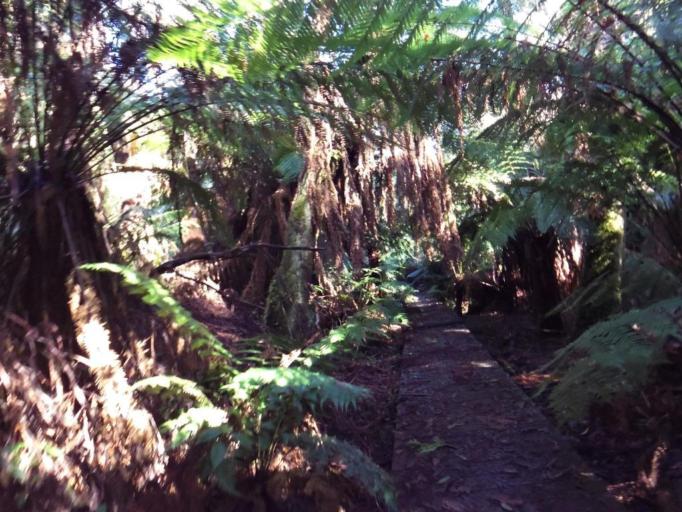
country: AU
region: Victoria
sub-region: Cardinia
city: Emerald
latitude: -37.9194
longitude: 145.4356
